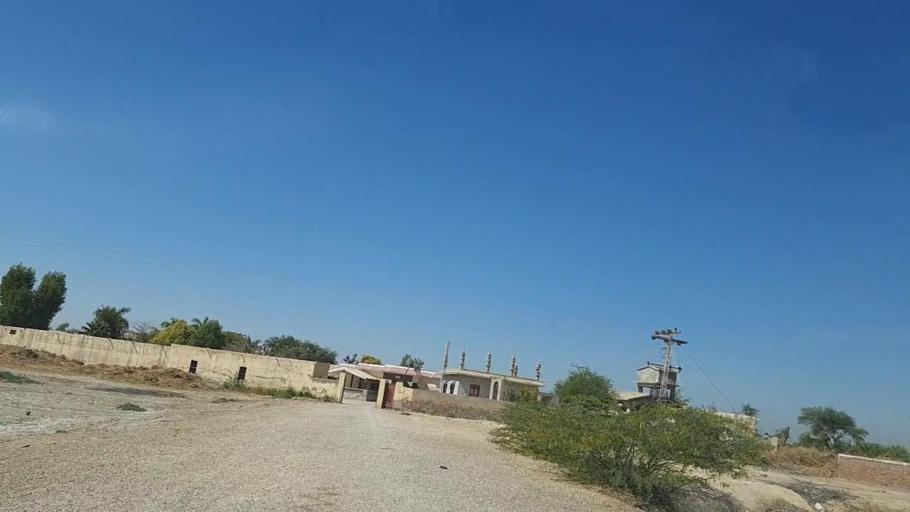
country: PK
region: Sindh
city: Dhoro Naro
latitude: 25.4864
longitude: 69.5267
